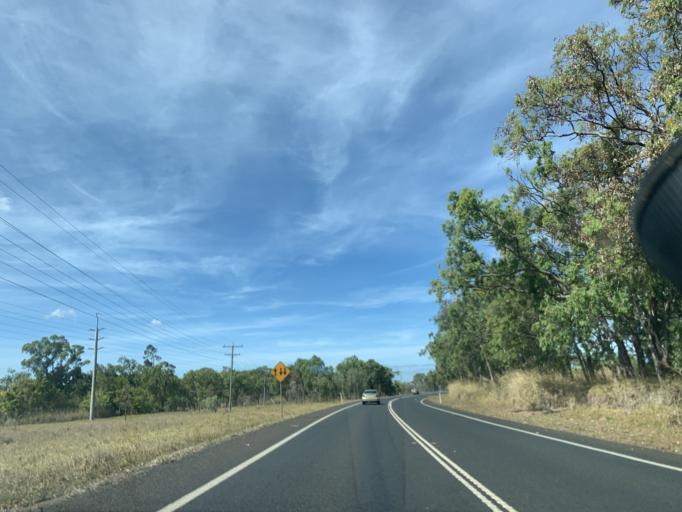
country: AU
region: Queensland
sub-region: Tablelands
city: Mareeba
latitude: -17.1090
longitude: 145.4311
